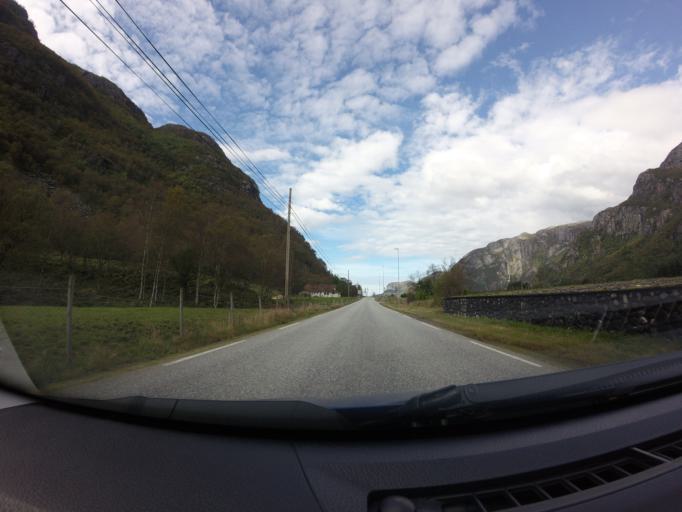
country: NO
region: Rogaland
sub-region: Forsand
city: Forsand
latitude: 58.8272
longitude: 6.1892
